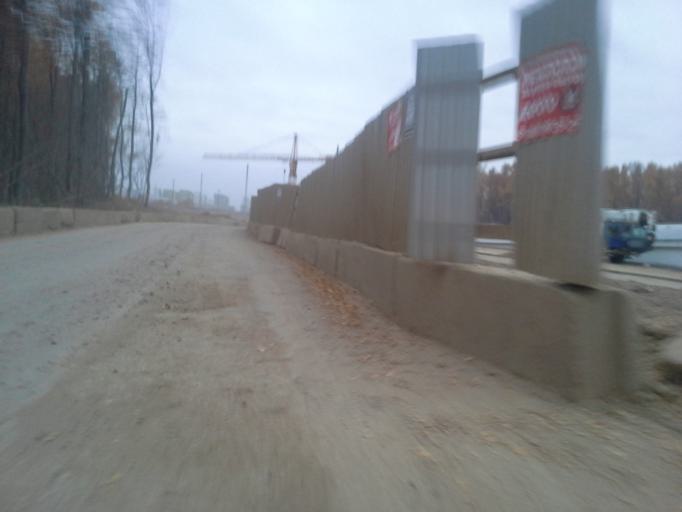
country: RU
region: Moskovskaya
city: Kommunarka
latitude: 55.5590
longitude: 37.4720
